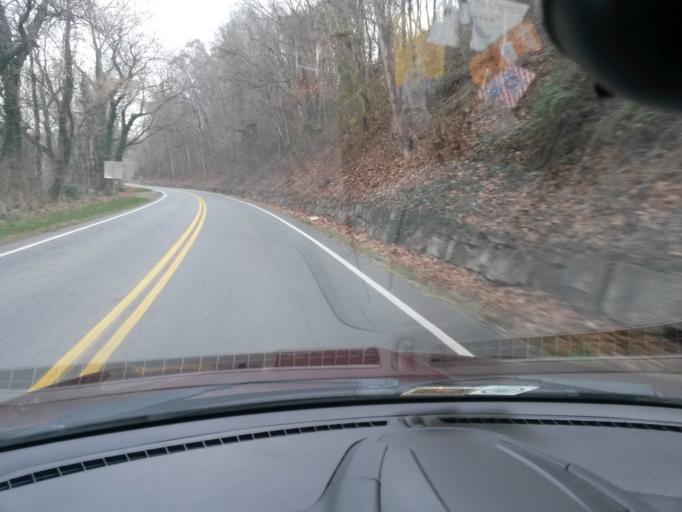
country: US
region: Virginia
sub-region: Alleghany County
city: Clifton Forge
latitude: 37.8107
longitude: -79.8119
